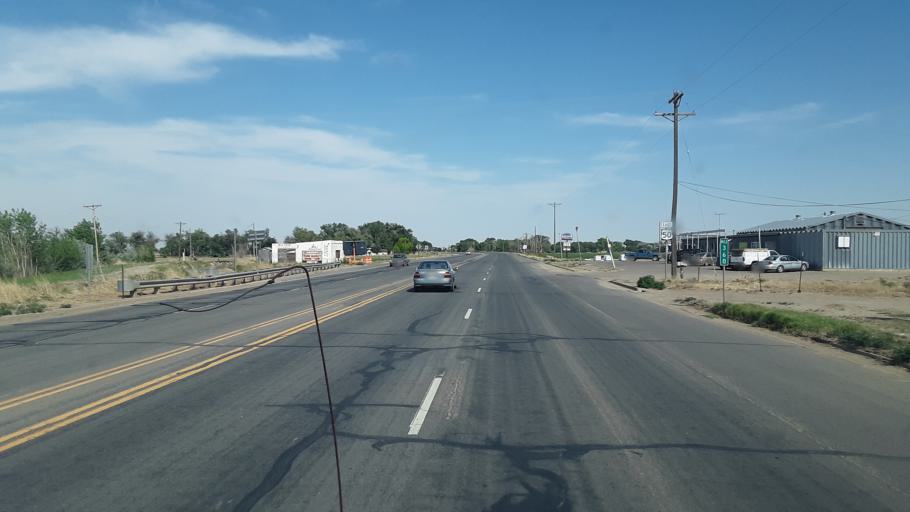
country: US
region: Colorado
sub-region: Otero County
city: Rocky Ford
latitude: 38.1063
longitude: -103.8622
